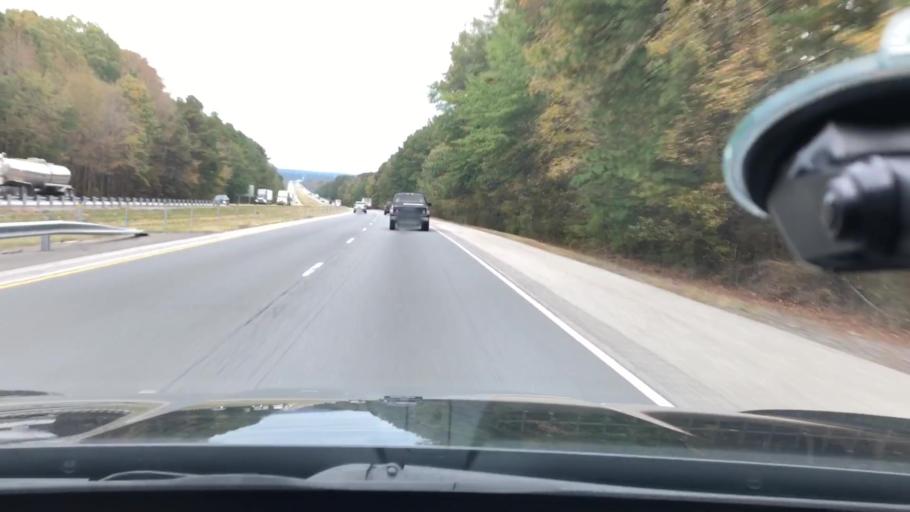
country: US
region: Arkansas
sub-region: Clark County
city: Arkadelphia
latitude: 34.1428
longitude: -93.0801
